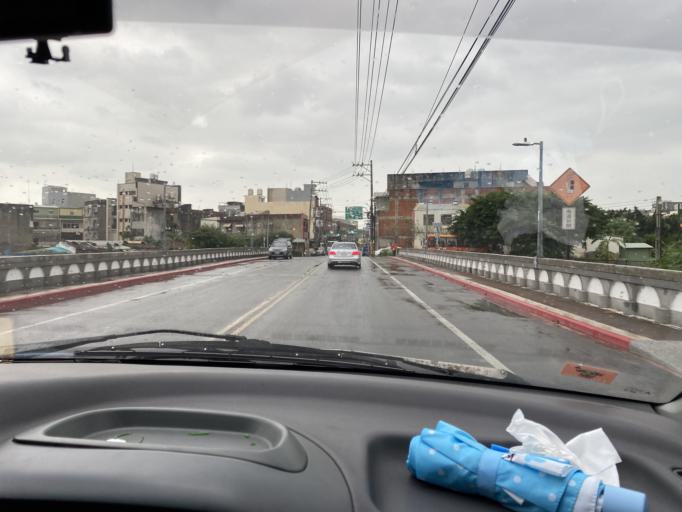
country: TW
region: Taiwan
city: Taoyuan City
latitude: 25.0590
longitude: 121.1988
